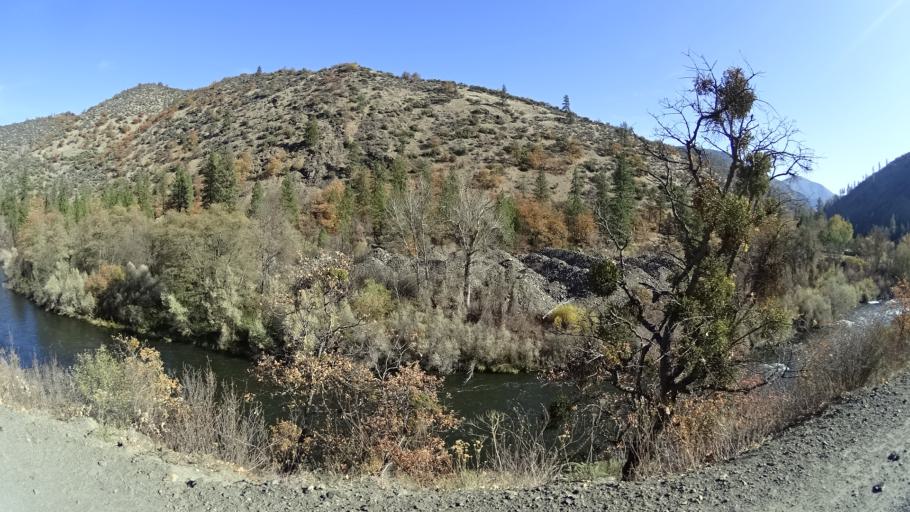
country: US
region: California
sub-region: Siskiyou County
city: Yreka
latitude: 41.8499
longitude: -122.6953
